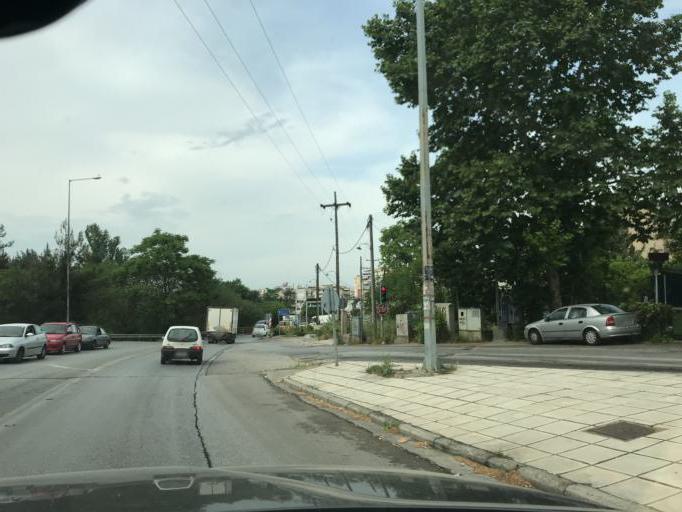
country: GR
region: Central Macedonia
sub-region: Nomos Thessalonikis
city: Sykies
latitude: 40.6575
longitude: 22.9648
